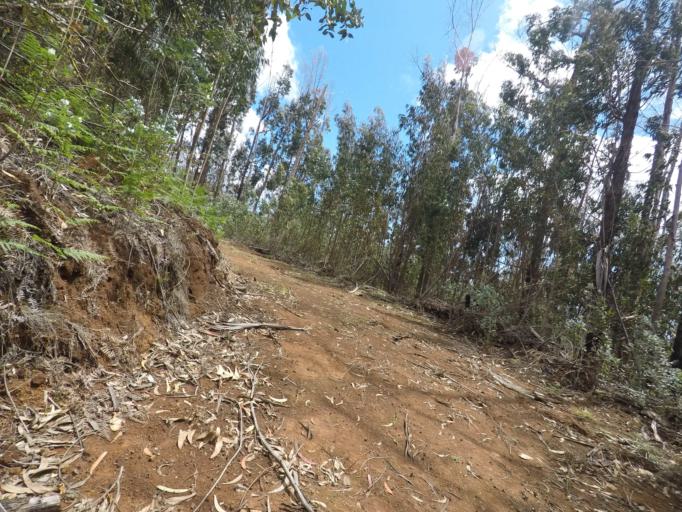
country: PT
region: Madeira
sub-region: Calheta
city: Estreito da Calheta
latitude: 32.7483
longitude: -17.1957
